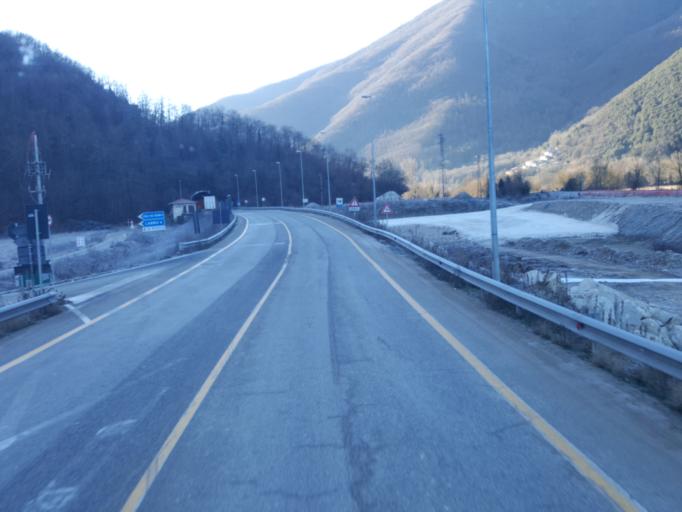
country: IT
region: Latium
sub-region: Provincia di Rieti
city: Colli sul Velino
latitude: 42.5051
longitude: 12.7466
